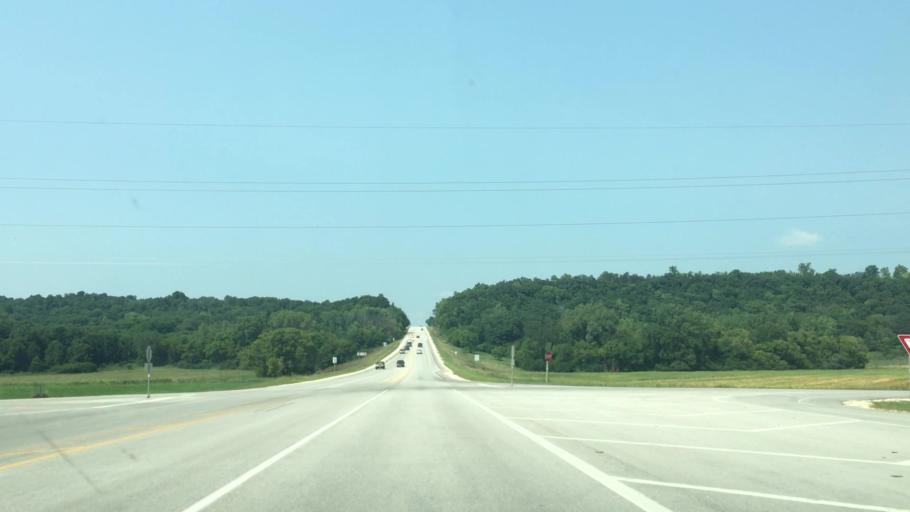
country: US
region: Iowa
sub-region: Winneshiek County
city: Decorah
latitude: 43.3200
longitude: -91.8139
